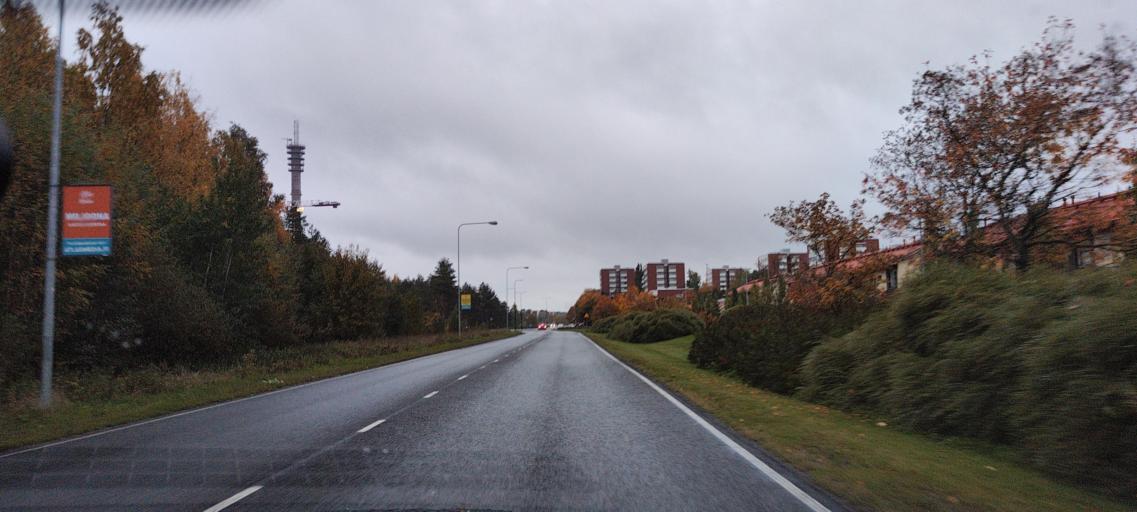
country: FI
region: Varsinais-Suomi
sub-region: Turku
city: Kaarina
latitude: 60.4528
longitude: 22.3320
